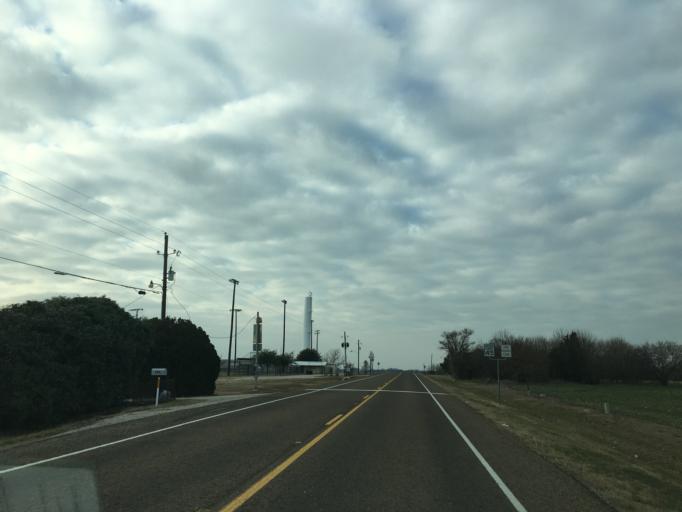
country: US
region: Texas
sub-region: Ellis County
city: Palmer
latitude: 32.4319
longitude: -96.6830
